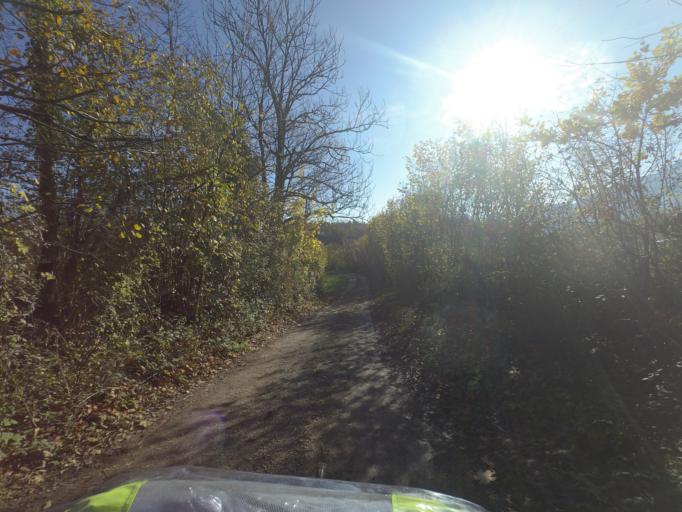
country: AT
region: Salzburg
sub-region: Politischer Bezirk Hallein
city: Adnet
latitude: 47.6720
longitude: 13.1462
